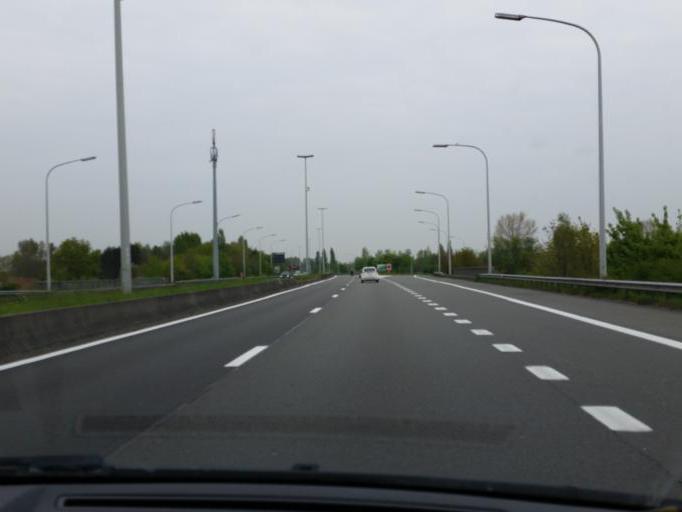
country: BE
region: Flanders
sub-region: Provincie Oost-Vlaanderen
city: Laarne
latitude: 51.0326
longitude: 3.8250
